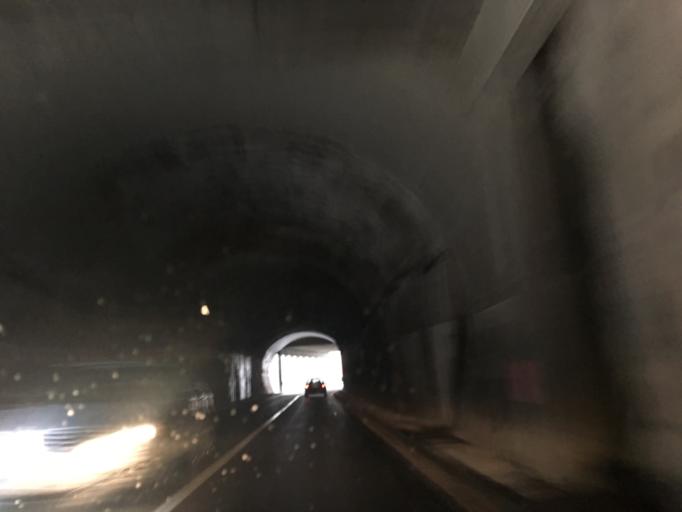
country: RS
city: Sokolovo Brdo
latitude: 43.1679
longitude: 19.7714
